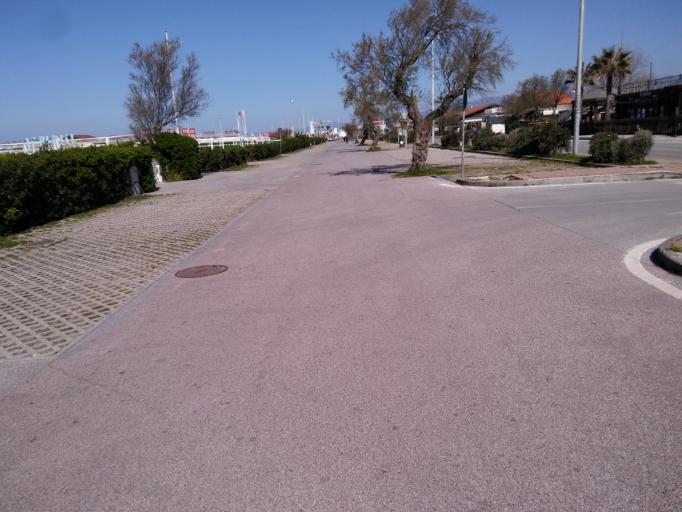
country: IT
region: Tuscany
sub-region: Provincia di Lucca
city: Viareggio
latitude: 43.8501
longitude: 10.2457
